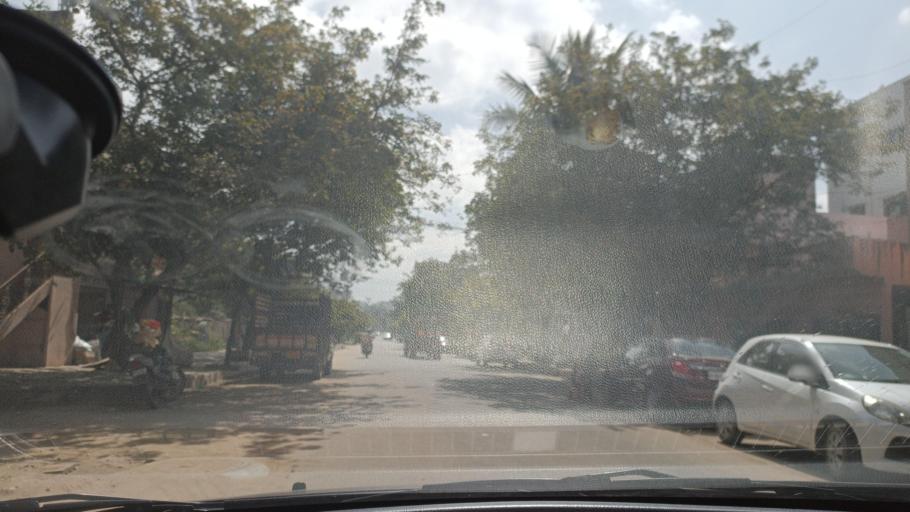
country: IN
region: Karnataka
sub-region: Bangalore Urban
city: Yelahanka
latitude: 13.0393
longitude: 77.6296
